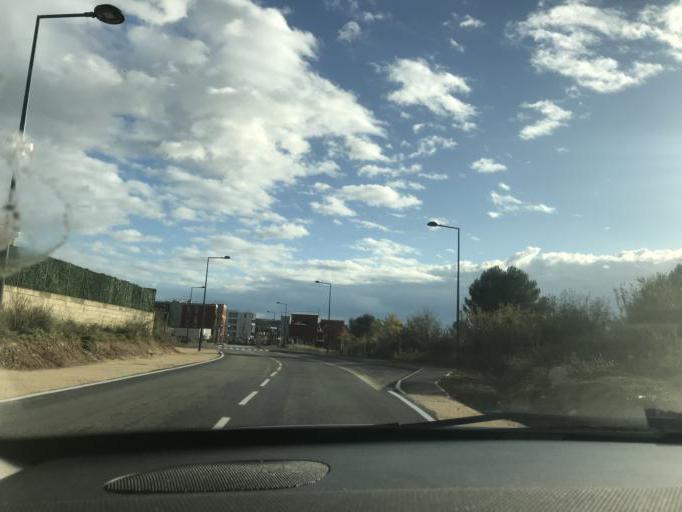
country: FR
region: Provence-Alpes-Cote d'Azur
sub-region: Departement des Bouches-du-Rhone
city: Vitrolles
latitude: 43.4584
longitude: 5.2287
